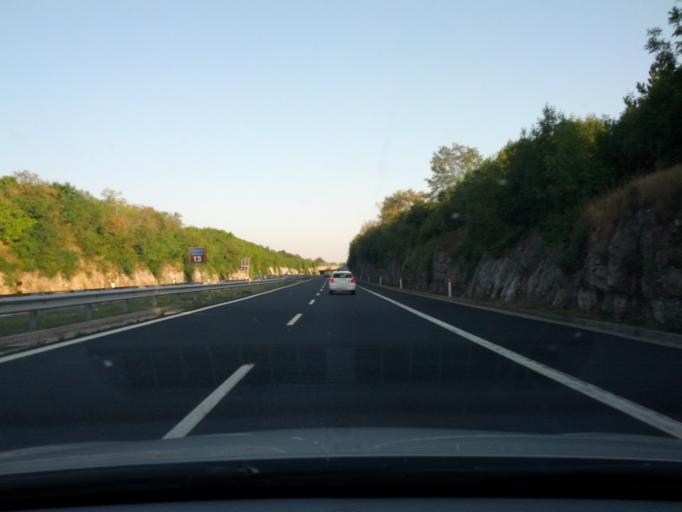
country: IT
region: Friuli Venezia Giulia
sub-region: Provincia di Trieste
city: Villa Opicina
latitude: 45.6720
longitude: 13.8210
